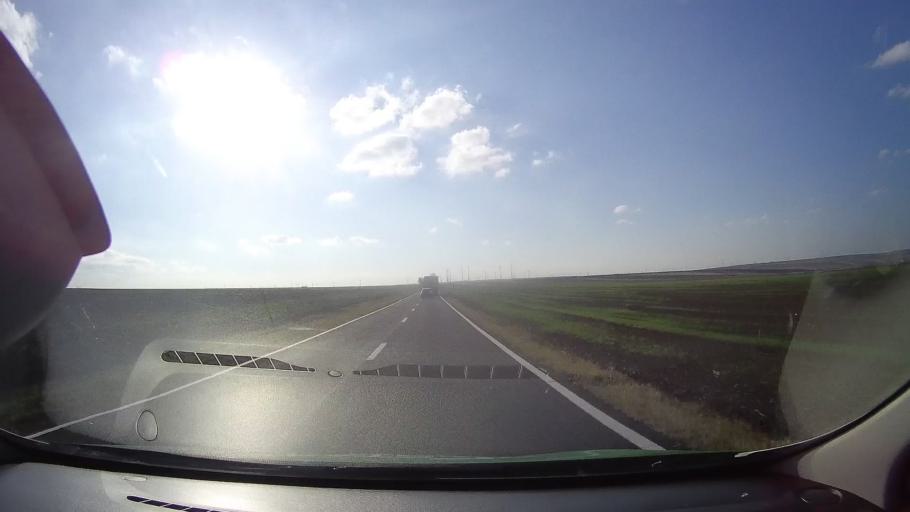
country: RO
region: Tulcea
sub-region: Comuna Topolog
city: Topolog
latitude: 44.8443
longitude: 28.3118
